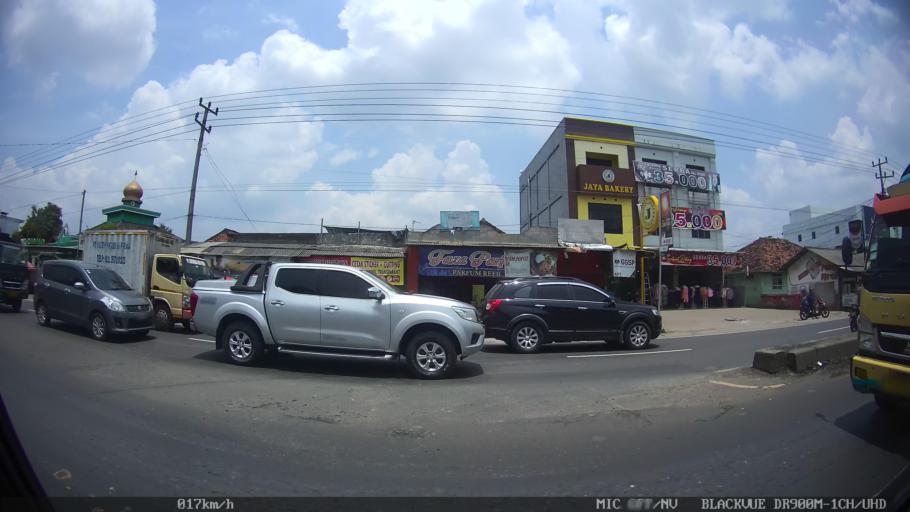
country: ID
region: Lampung
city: Natar
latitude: -5.3133
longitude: 105.1952
